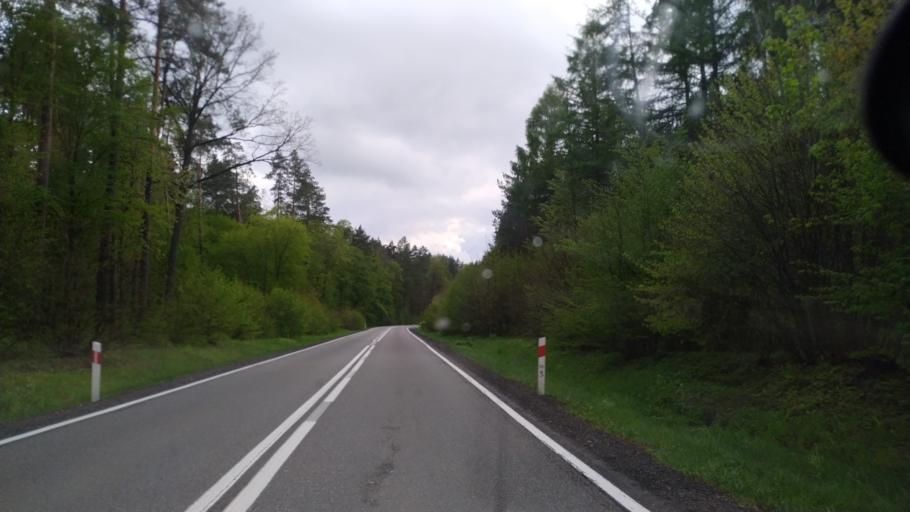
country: PL
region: Pomeranian Voivodeship
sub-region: Powiat kwidzynski
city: Ryjewo
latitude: 53.8142
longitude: 18.9766
